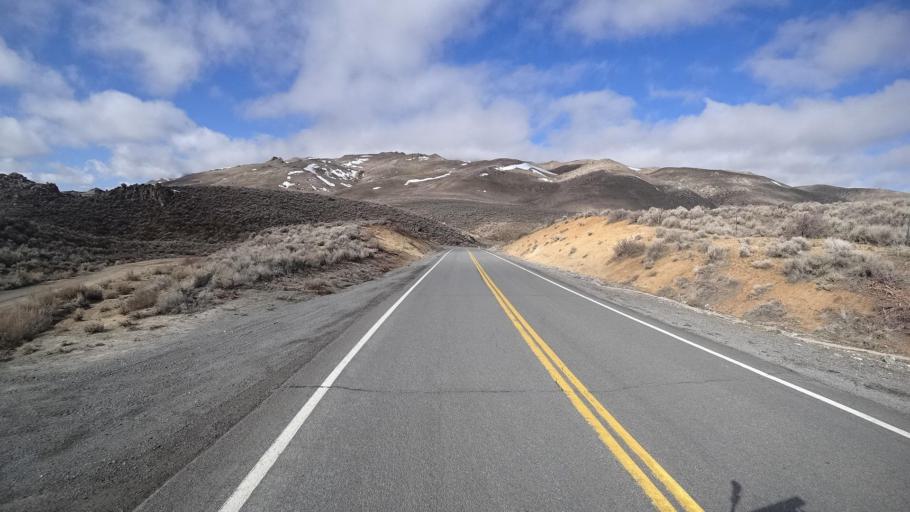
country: US
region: Nevada
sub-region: Washoe County
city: Cold Springs
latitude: 39.8034
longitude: -119.9282
